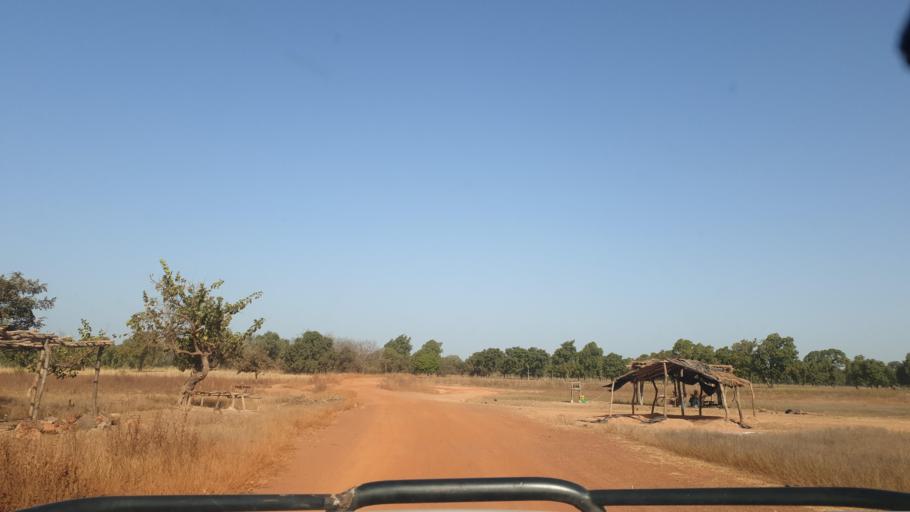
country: ML
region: Sikasso
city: Kolondieba
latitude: 11.7338
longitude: -6.8916
